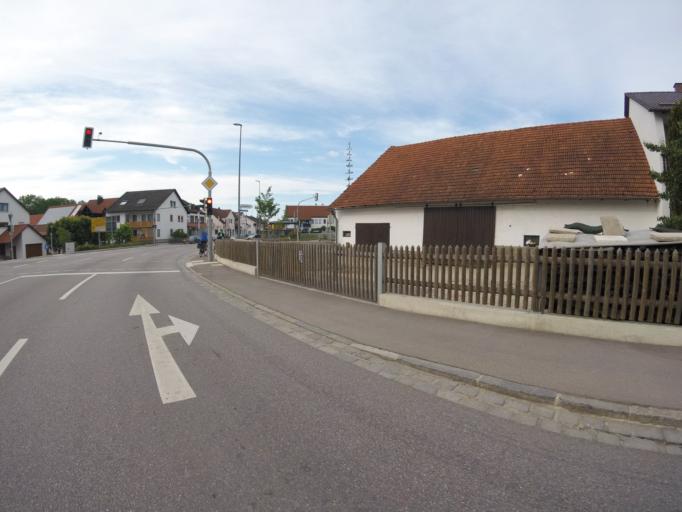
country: DE
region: Bavaria
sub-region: Upper Bavaria
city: Reichertshausen
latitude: 48.4661
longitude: 11.5082
